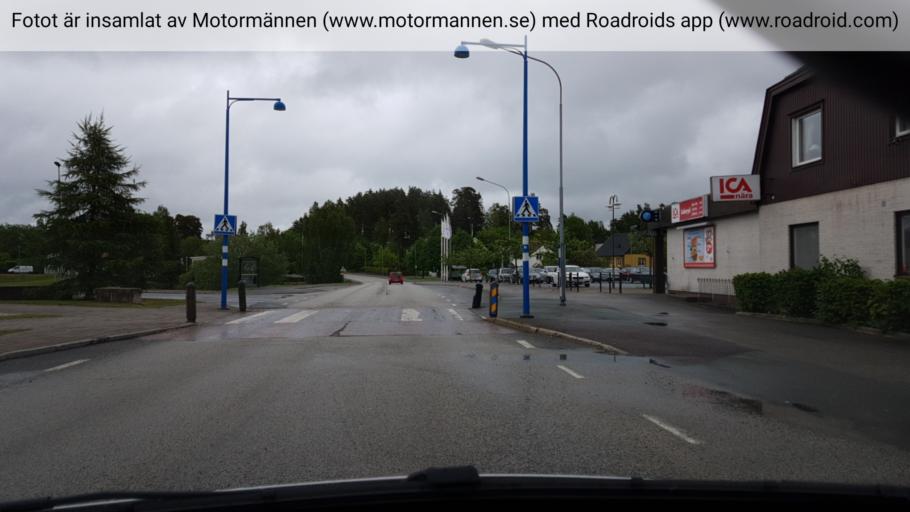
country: SE
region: Joenkoeping
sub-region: Jonkopings Kommun
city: Tenhult
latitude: 57.7738
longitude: 14.4176
